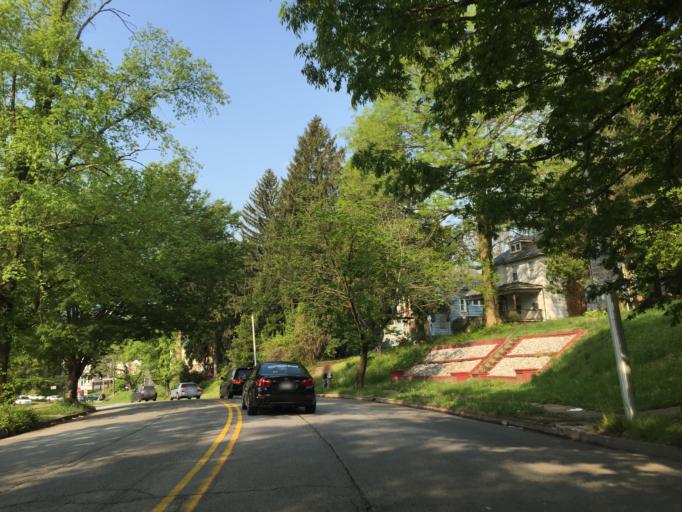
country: US
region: Maryland
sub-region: Baltimore County
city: Woodlawn
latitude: 39.3140
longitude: -76.6817
